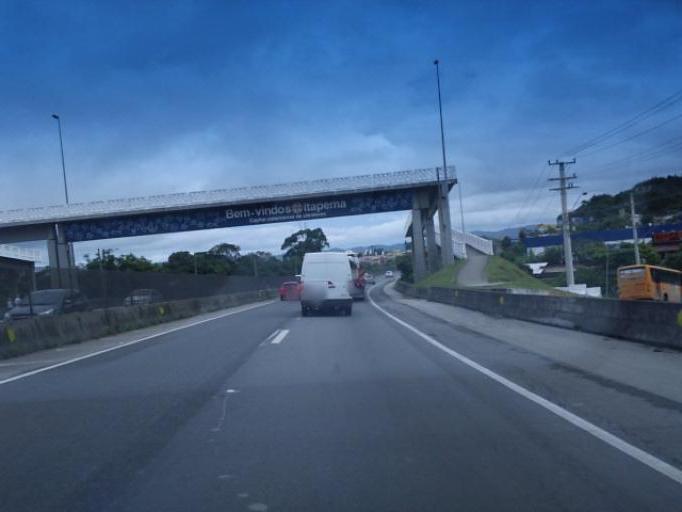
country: BR
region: Santa Catarina
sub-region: Itapema
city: Itapema
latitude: -27.0581
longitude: -48.5976
